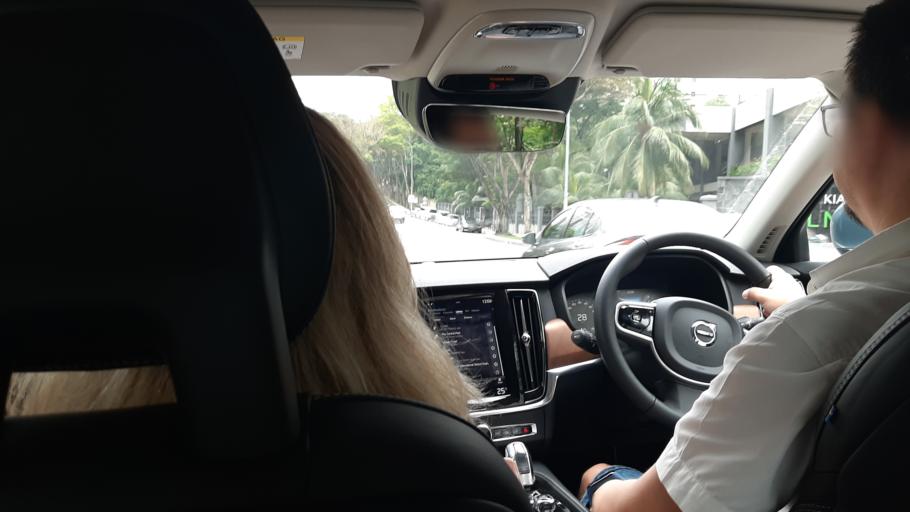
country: MY
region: Kuala Lumpur
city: Kuala Lumpur
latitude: 3.1673
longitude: 101.6526
